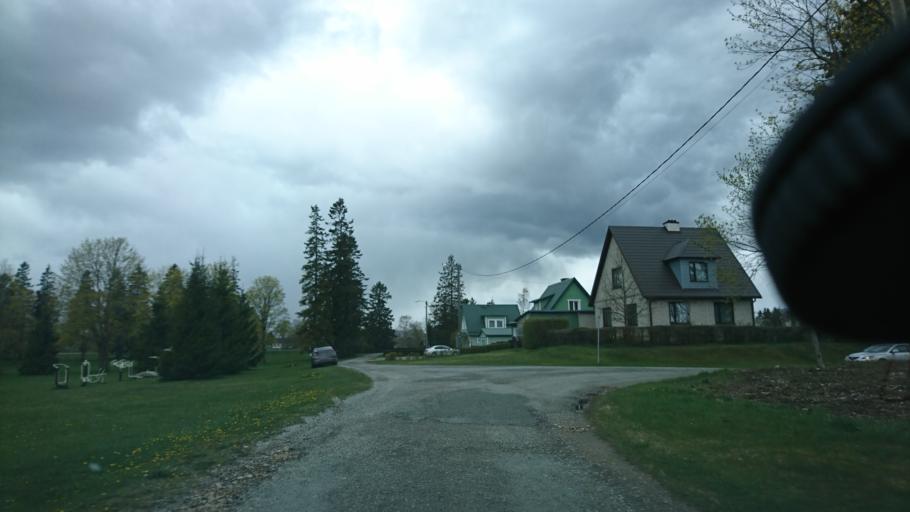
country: EE
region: Laeaene-Virumaa
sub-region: Tapa vald
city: Tapa
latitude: 59.2570
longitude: 25.9653
